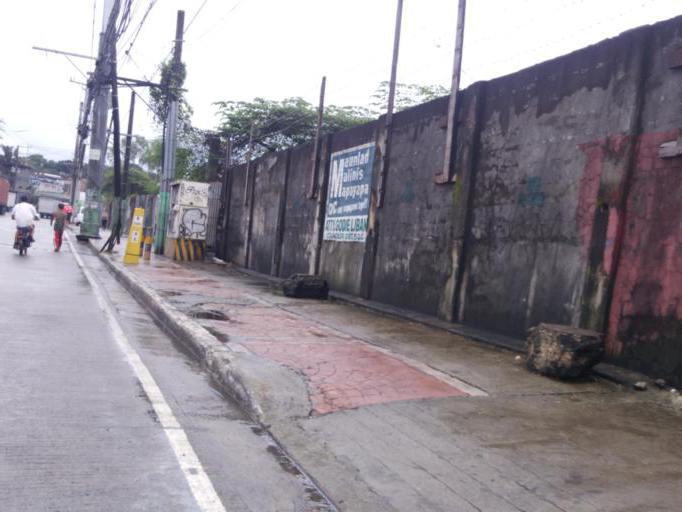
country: PH
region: Calabarzon
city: Bagong Pagasa
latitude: 14.7272
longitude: 121.0415
